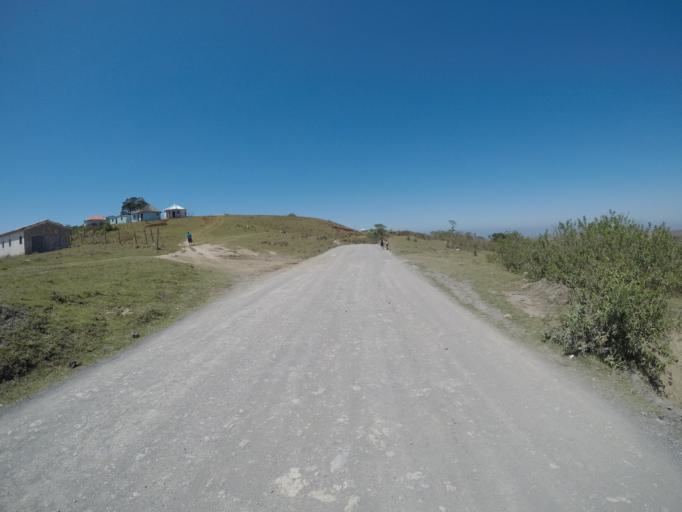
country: ZA
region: Eastern Cape
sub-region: OR Tambo District Municipality
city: Libode
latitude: -31.9860
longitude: 29.0518
